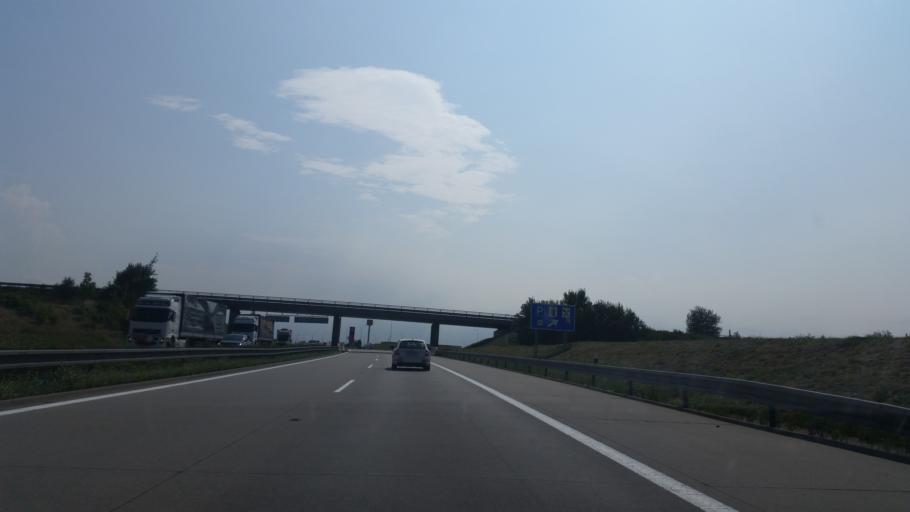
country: CZ
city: Klimkovice
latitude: 49.7803
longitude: 18.0993
